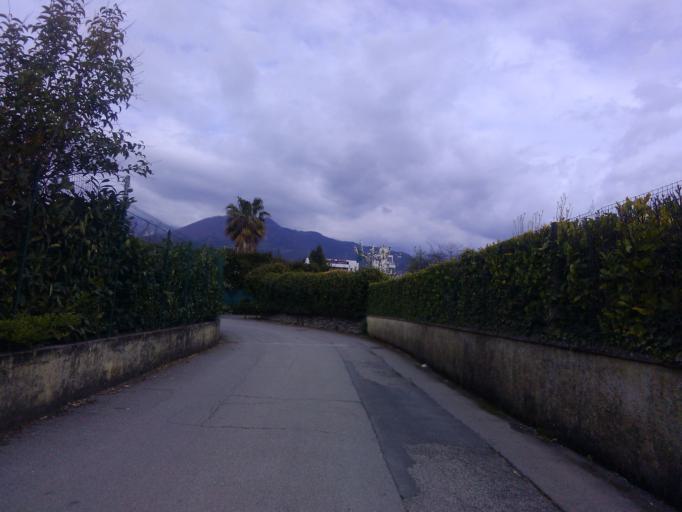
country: IT
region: Tuscany
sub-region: Provincia di Massa-Carrara
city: Massa
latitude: 44.0241
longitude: 10.0961
